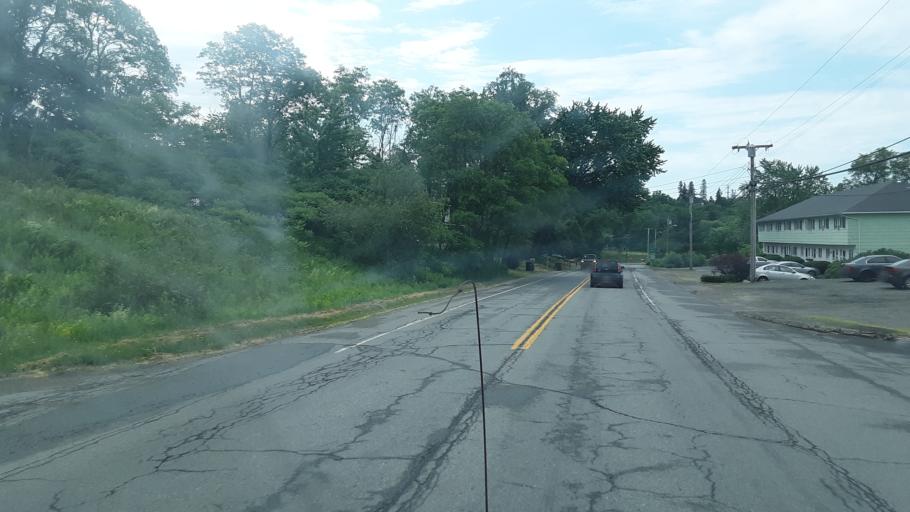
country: US
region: Maine
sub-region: Penobscot County
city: Eddington
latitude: 44.8266
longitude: -68.6936
